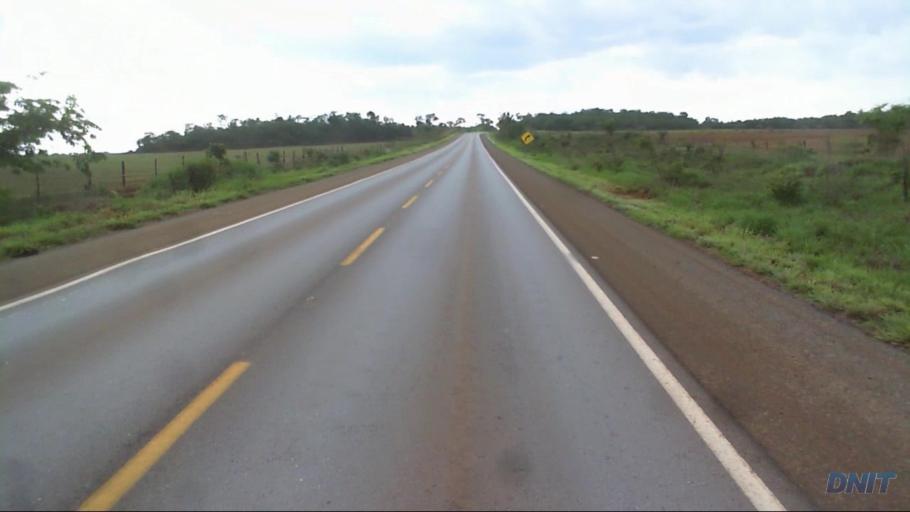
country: BR
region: Goias
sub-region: Uruacu
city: Uruacu
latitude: -14.6741
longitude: -49.1422
